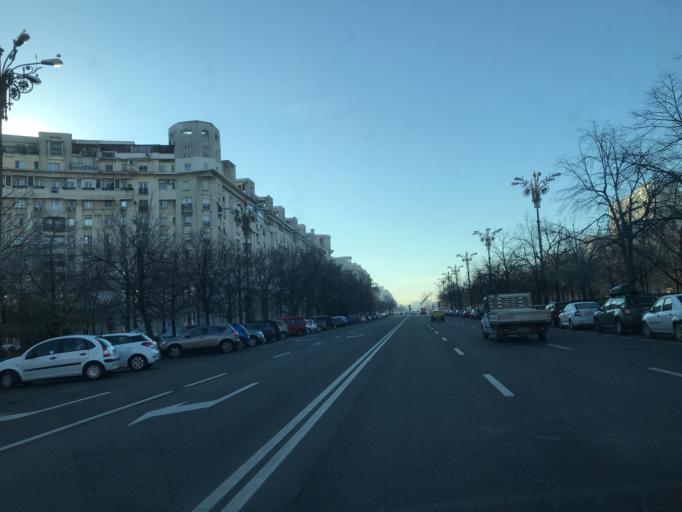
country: RO
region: Bucuresti
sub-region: Municipiul Bucuresti
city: Bucuresti
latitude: 44.4328
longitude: 26.0913
